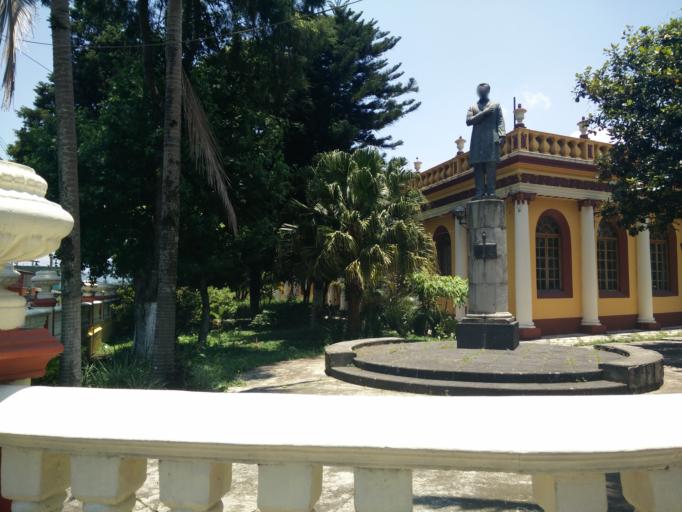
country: MX
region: Veracruz
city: Coatepec
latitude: 19.4543
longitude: -96.9604
